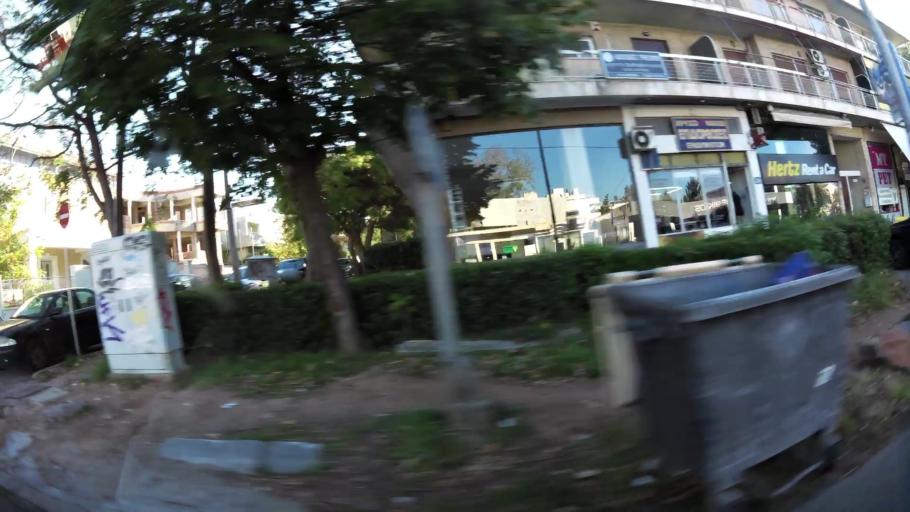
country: GR
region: Attica
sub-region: Nomarchia Athinas
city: Kifisia
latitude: 38.0808
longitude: 23.8146
